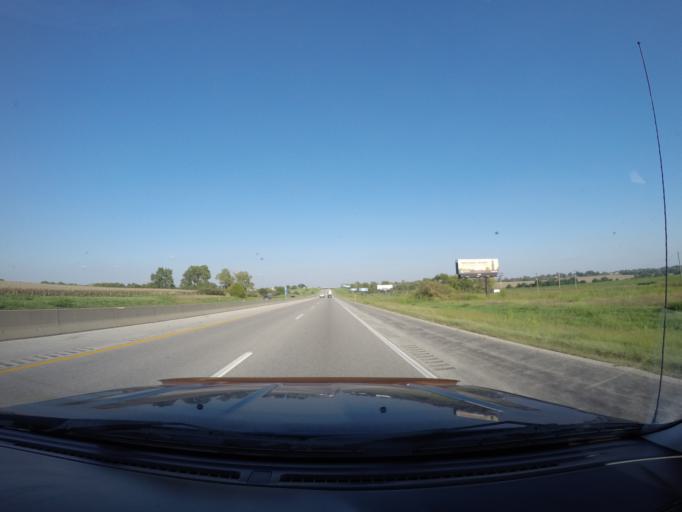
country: US
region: Kansas
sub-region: Leavenworth County
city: Basehor
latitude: 39.0806
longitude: -94.9588
